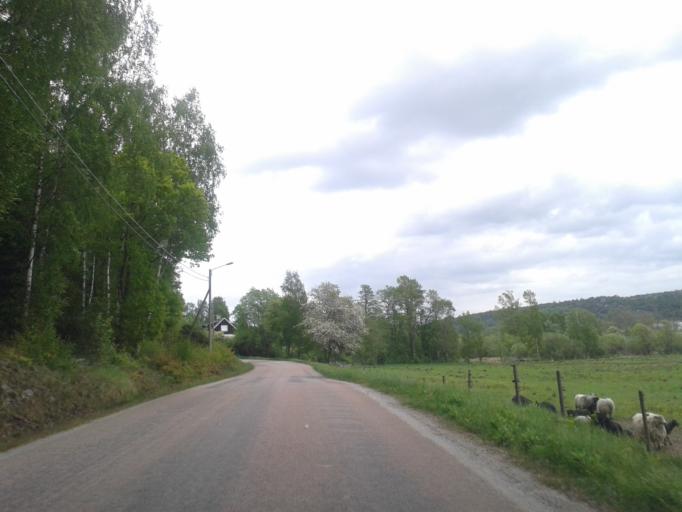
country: SE
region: Vaestra Goetaland
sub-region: Kungalvs Kommun
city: Kungalv
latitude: 57.8700
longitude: 12.0119
